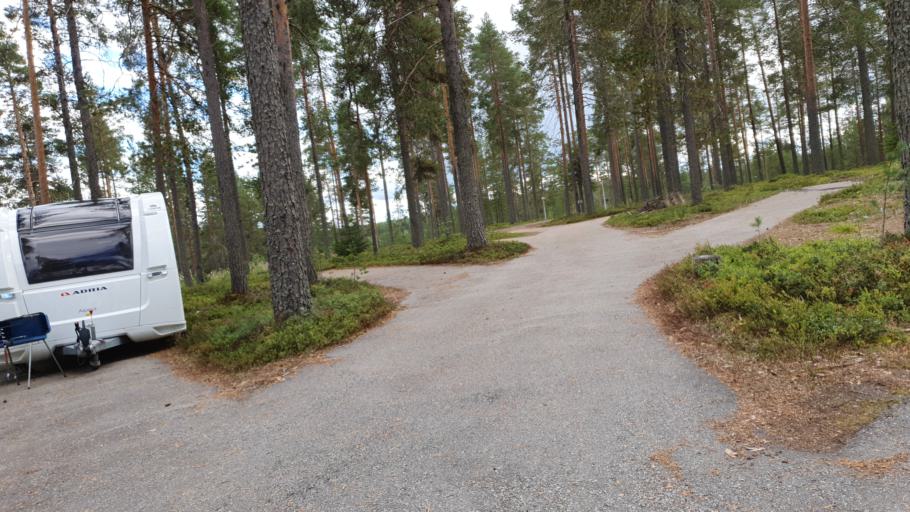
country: FI
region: Kainuu
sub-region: Kehys-Kainuu
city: Kuhmo
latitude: 64.1157
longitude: 29.5910
